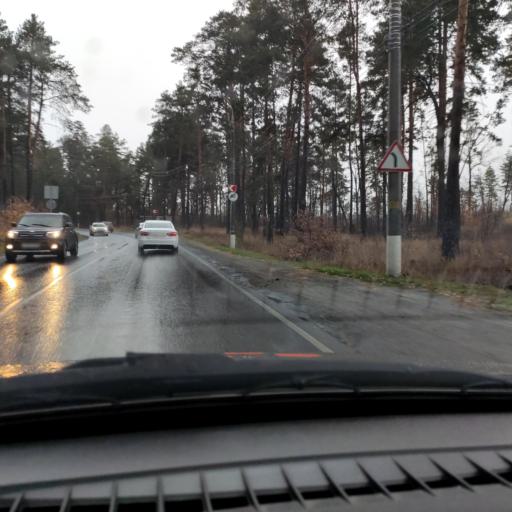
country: RU
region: Samara
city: Tol'yatti
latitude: 53.4871
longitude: 49.3112
